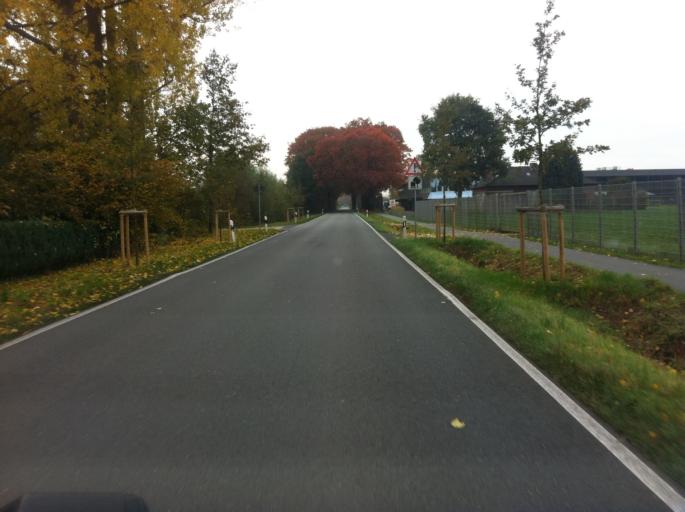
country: DE
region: North Rhine-Westphalia
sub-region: Regierungsbezirk Munster
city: Vreden
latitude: 52.0220
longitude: 6.8056
